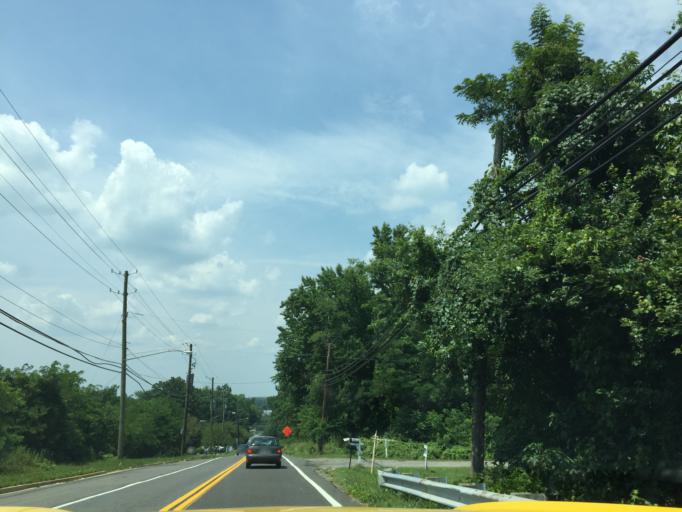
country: US
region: Maryland
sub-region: Prince George's County
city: Friendly
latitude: 38.7228
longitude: -76.9872
